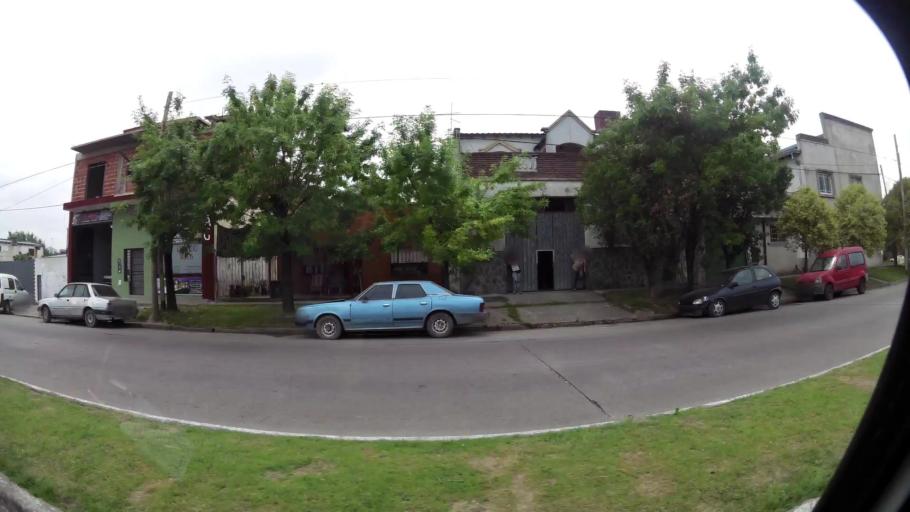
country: AR
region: Buenos Aires
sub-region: Partido de La Plata
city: La Plata
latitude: -34.9032
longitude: -57.9929
